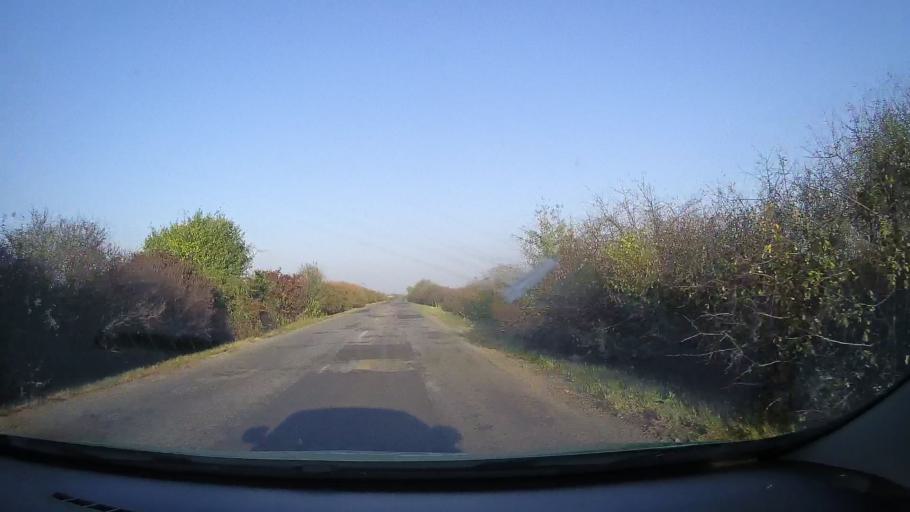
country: RO
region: Arad
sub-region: Comuna Tarnova
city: Tarnova
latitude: 46.3135
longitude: 21.7590
